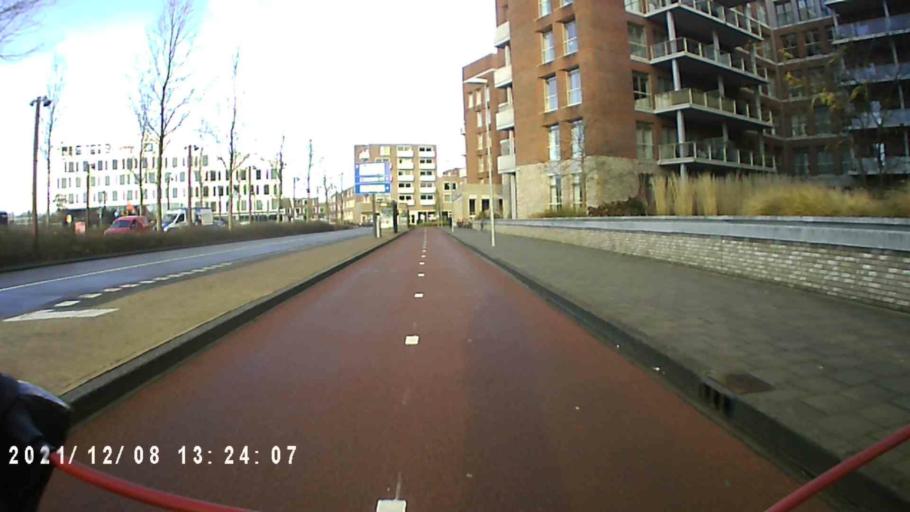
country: NL
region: Groningen
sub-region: Gemeente Groningen
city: Oosterpark
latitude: 53.2045
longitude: 6.5878
